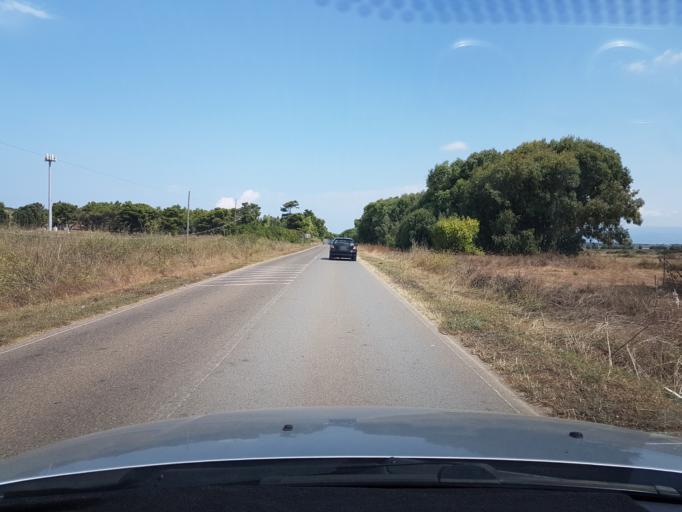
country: IT
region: Sardinia
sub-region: Provincia di Oristano
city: Cabras
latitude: 39.8917
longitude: 8.4350
